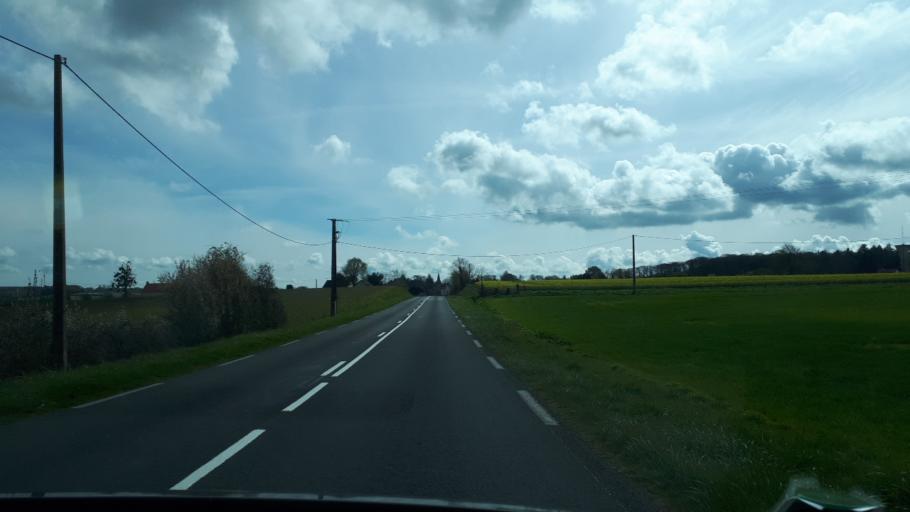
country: FR
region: Pays de la Loire
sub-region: Departement de la Sarthe
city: Le Grand-Luce
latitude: 47.8695
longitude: 0.4533
